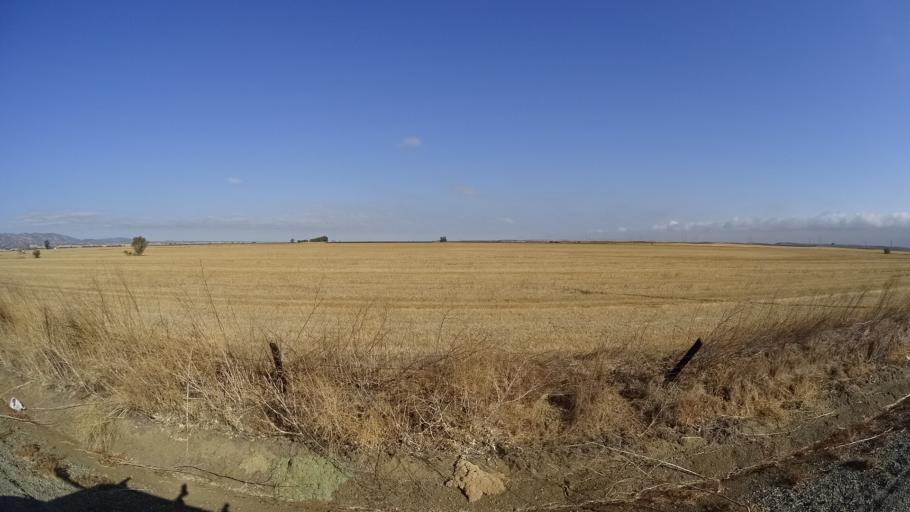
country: US
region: California
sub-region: Yolo County
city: Esparto
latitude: 38.7809
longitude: -122.0313
